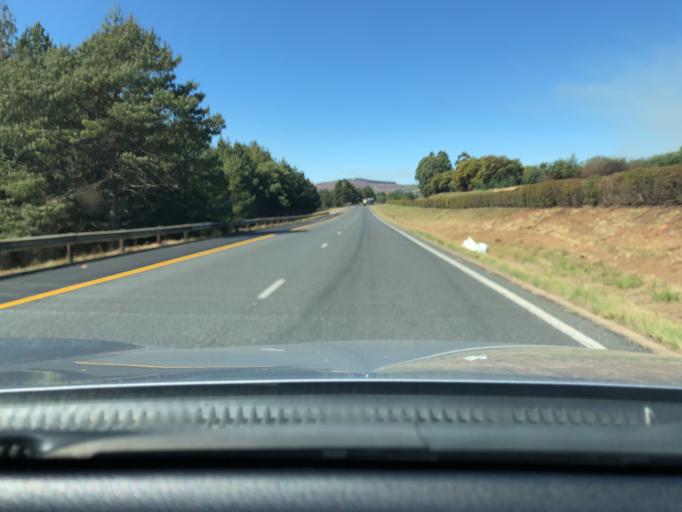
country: ZA
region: KwaZulu-Natal
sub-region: uMgungundlovu District Municipality
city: Mooirivier
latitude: -29.3449
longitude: 30.0834
